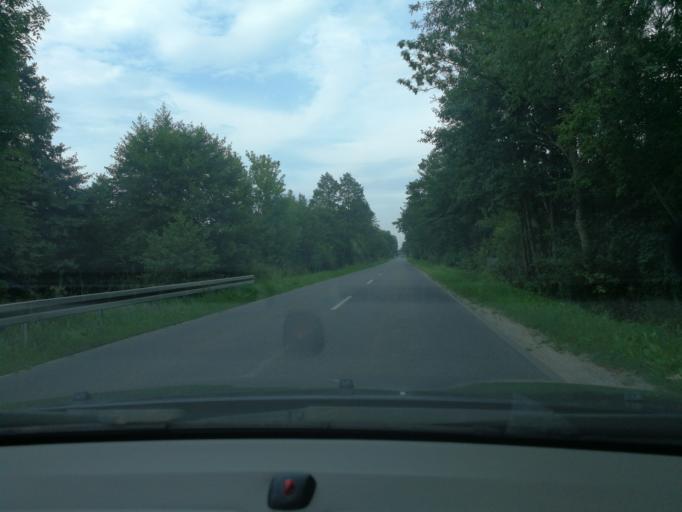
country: PL
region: Masovian Voivodeship
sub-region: Powiat grodziski
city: Grodzisk Mazowiecki
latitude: 52.1362
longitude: 20.6190
